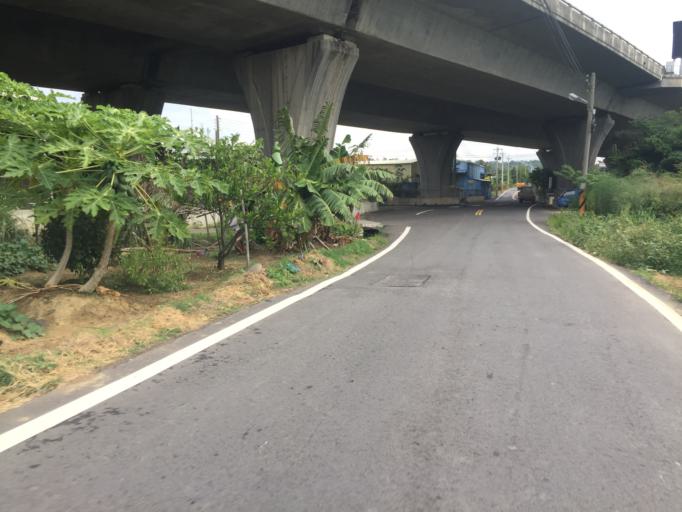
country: TW
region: Taiwan
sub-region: Hsinchu
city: Hsinchu
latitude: 24.7094
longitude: 120.8868
